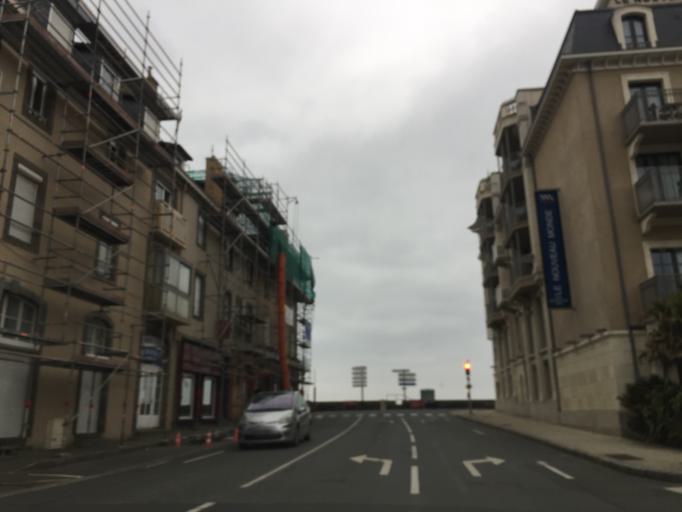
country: FR
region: Brittany
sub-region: Departement d'Ille-et-Vilaine
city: Saint-Malo
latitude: 48.6530
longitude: -2.0112
